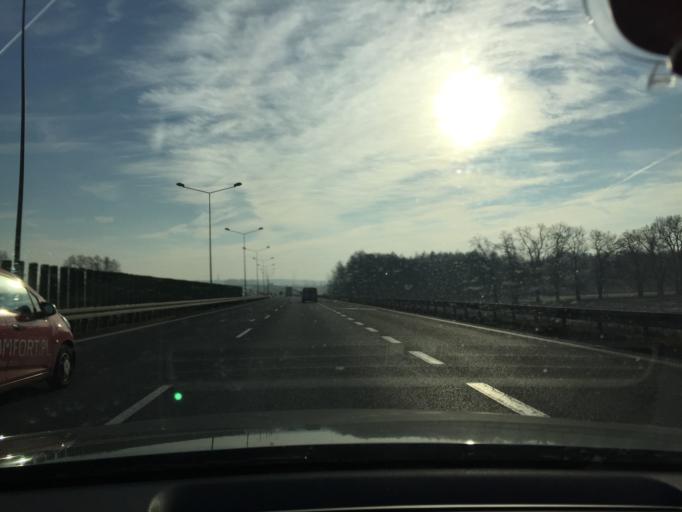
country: PL
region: Silesian Voivodeship
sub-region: Powiat gliwicki
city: Sosnicowice
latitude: 50.3080
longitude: 18.5517
